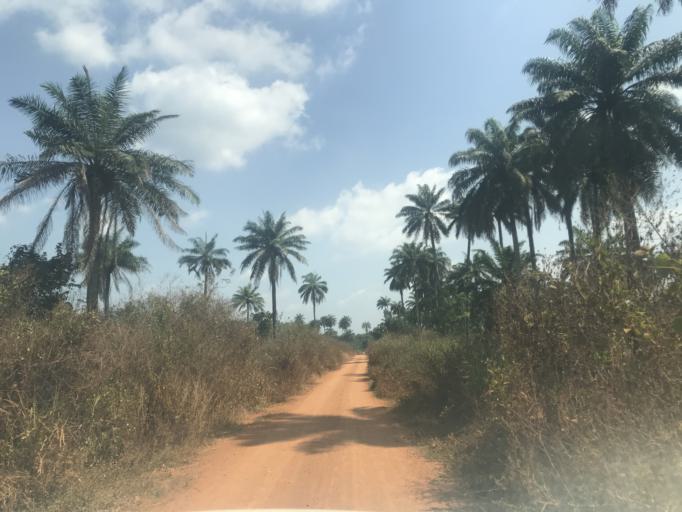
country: NG
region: Osun
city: Oke Mesi
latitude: 7.8934
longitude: 4.8732
